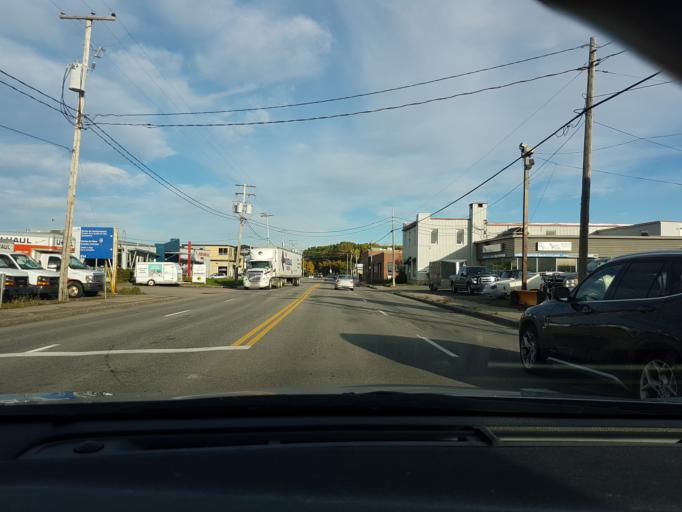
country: CA
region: Quebec
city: Quebec
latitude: 46.8046
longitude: -71.2647
